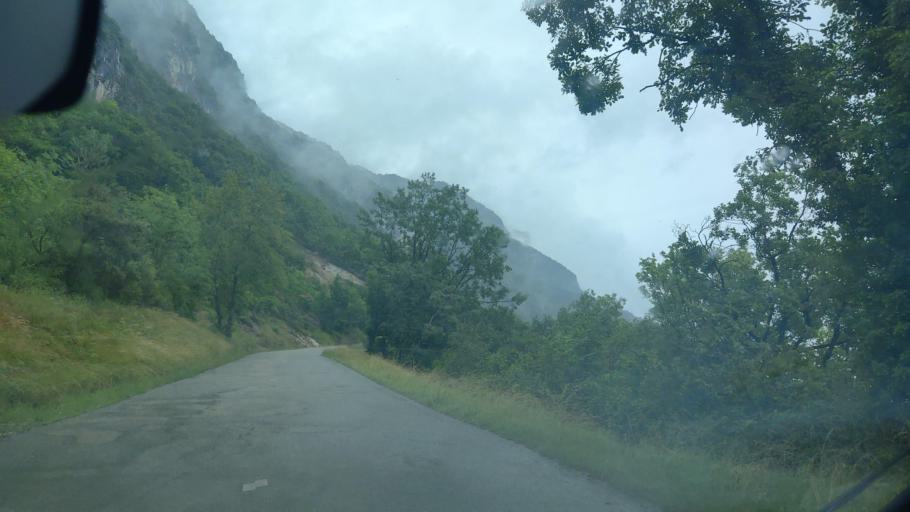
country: FR
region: Rhone-Alpes
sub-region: Departement de la Savoie
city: Chatillon
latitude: 45.8037
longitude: 5.8588
